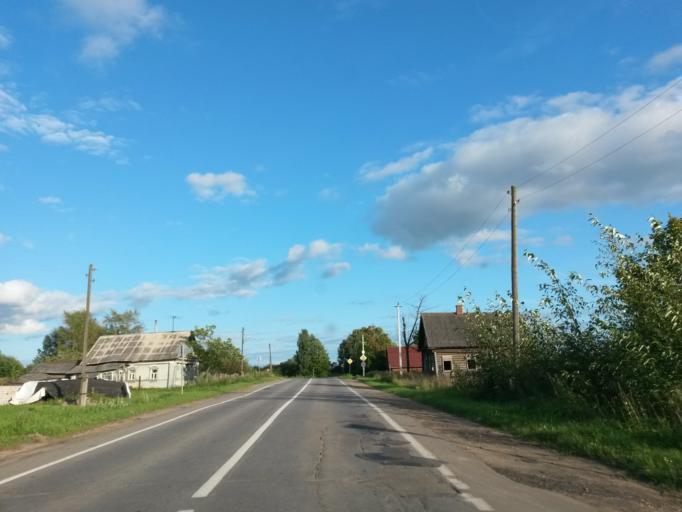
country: RU
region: Jaroslavl
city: Konstantinovskiy
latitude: 57.8464
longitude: 39.6398
